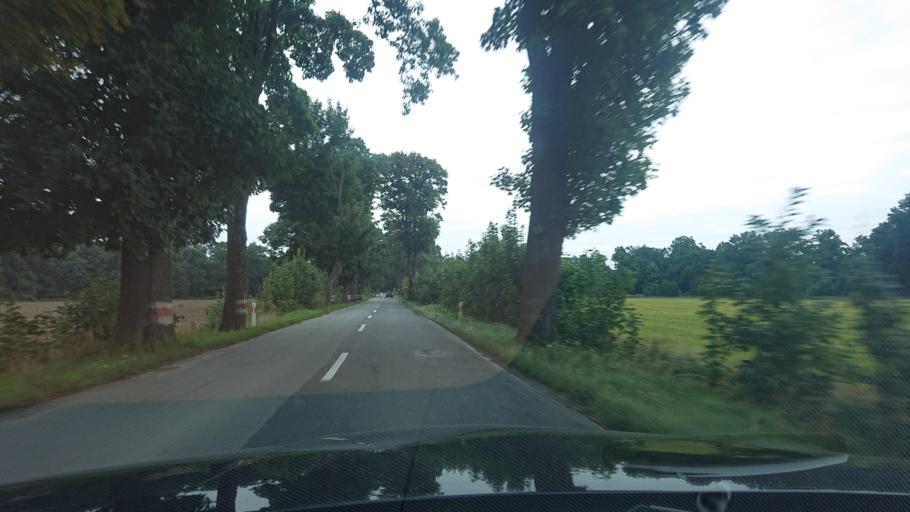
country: PL
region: Lower Silesian Voivodeship
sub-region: Powiat zabkowicki
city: Kamieniec Zabkowicki
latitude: 50.5087
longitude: 16.8701
